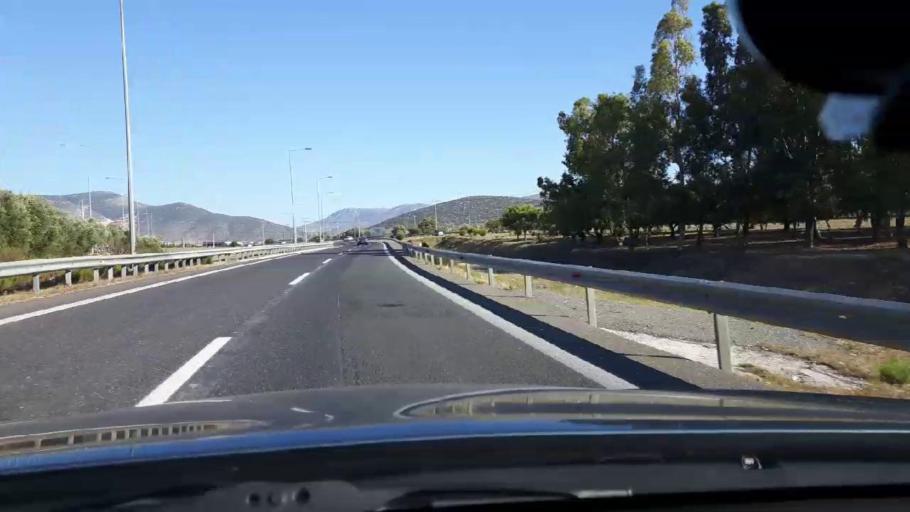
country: GR
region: Attica
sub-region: Nomarchia Anatolikis Attikis
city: Markopoulo
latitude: 37.8936
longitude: 23.9152
